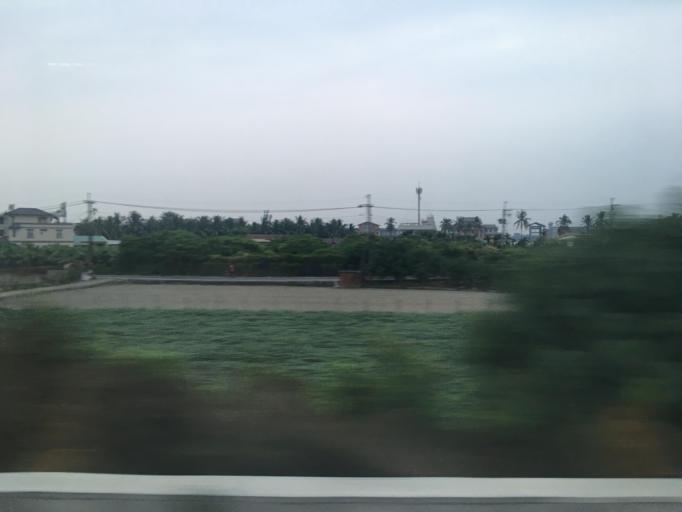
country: TW
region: Taiwan
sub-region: Pingtung
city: Pingtung
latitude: 22.6643
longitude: 120.4599
